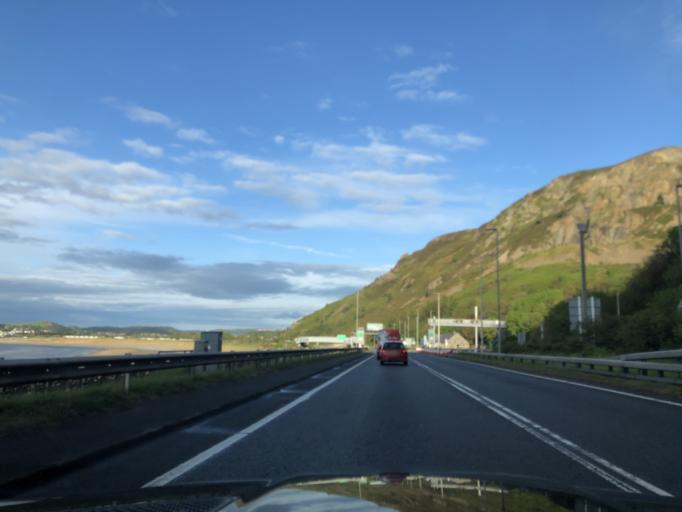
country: GB
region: Wales
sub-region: Conwy
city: Conwy
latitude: 53.2873
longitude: -3.8749
